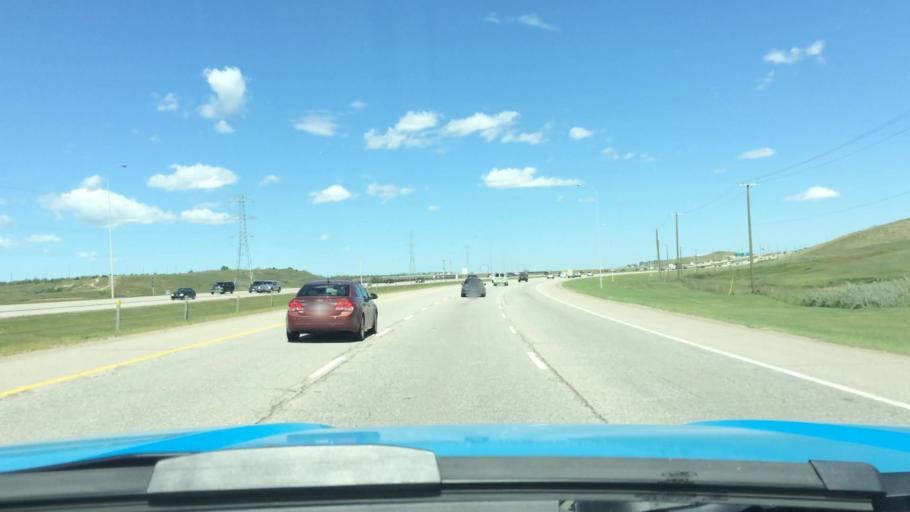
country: CA
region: Alberta
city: Calgary
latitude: 51.1289
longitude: -114.0457
